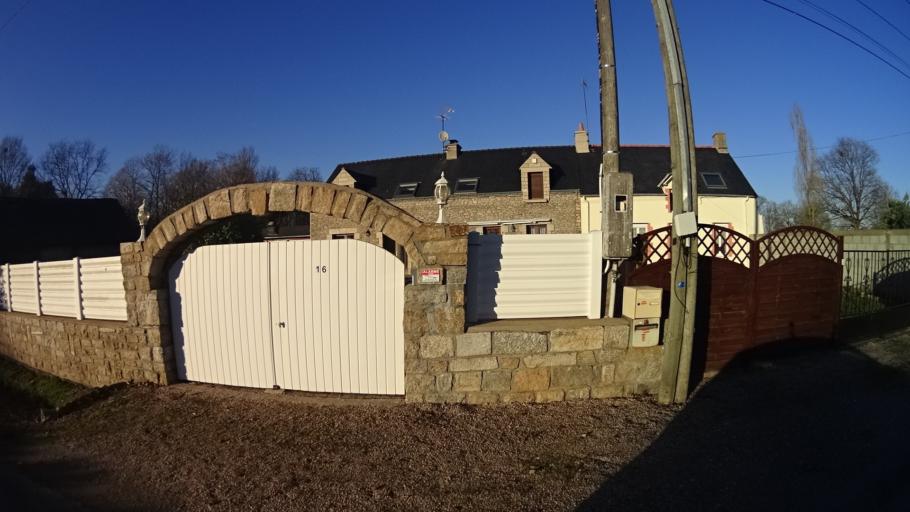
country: FR
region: Brittany
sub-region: Departement du Morbihan
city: Saint-Jean-la-Poterie
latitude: 47.6500
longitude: -2.1392
